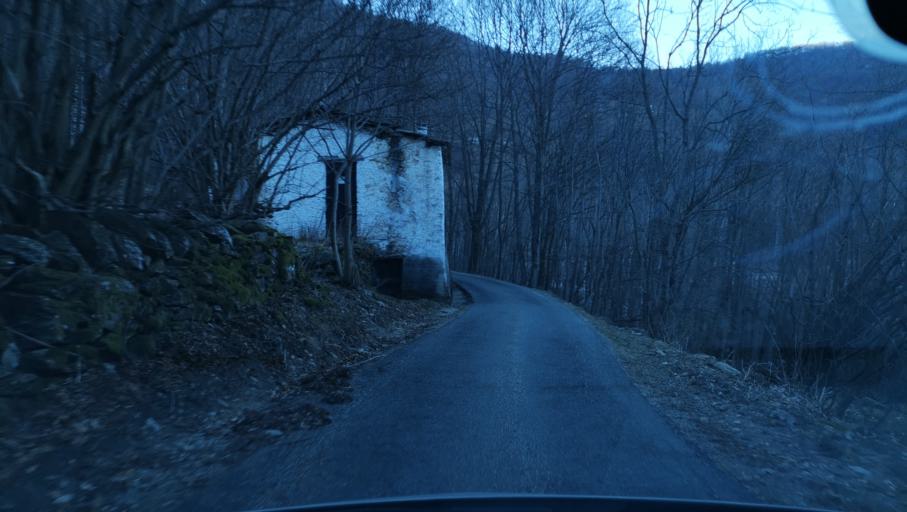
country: IT
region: Piedmont
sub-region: Provincia di Torino
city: Rora
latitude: 44.7844
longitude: 7.1888
